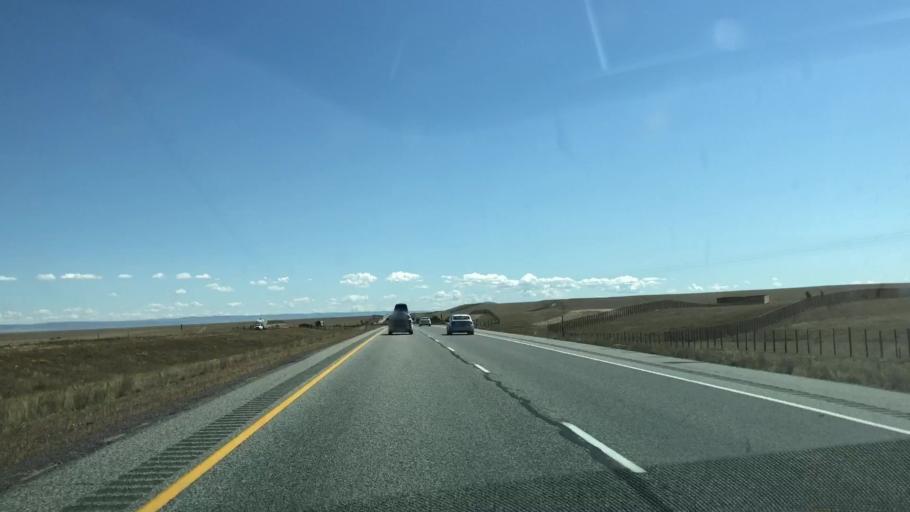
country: US
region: Wyoming
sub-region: Albany County
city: Laramie
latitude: 41.4863
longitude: -106.0287
